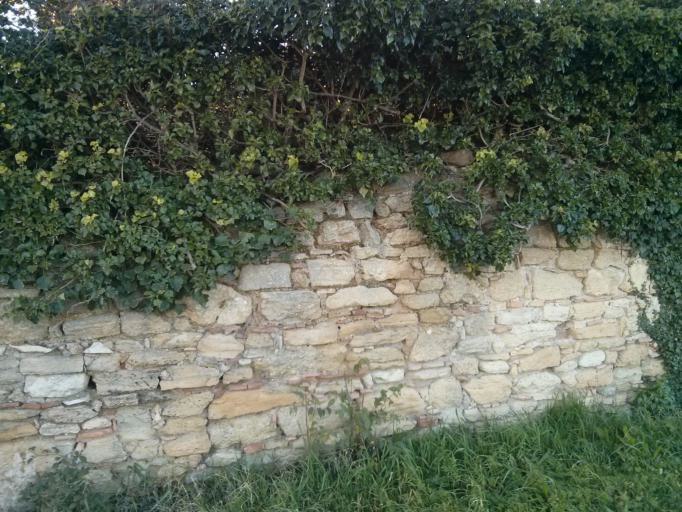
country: FR
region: Languedoc-Roussillon
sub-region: Departement du Gard
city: Aigues-Vives
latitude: 43.7327
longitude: 4.1818
